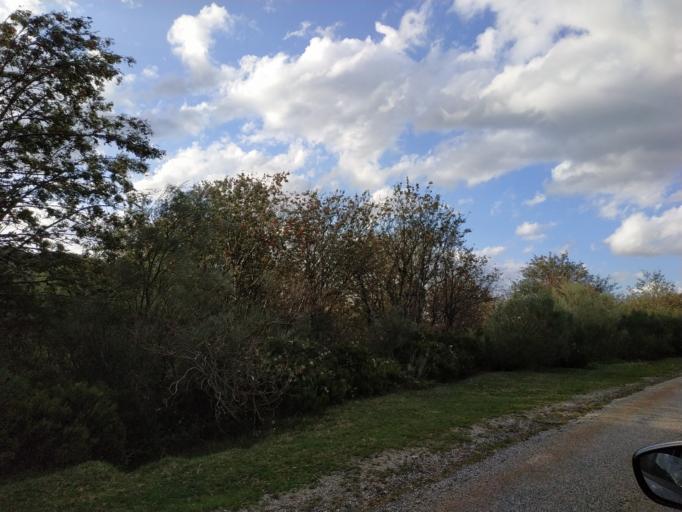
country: ES
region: Castille and Leon
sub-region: Provincia de Leon
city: Candin
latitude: 42.8759
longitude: -6.8312
